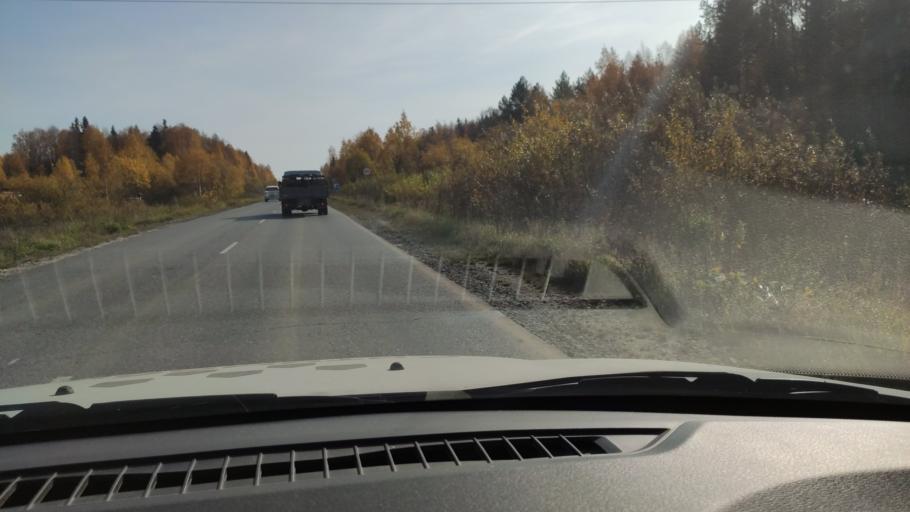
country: RU
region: Perm
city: Novyye Lyady
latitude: 58.0316
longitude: 56.6153
